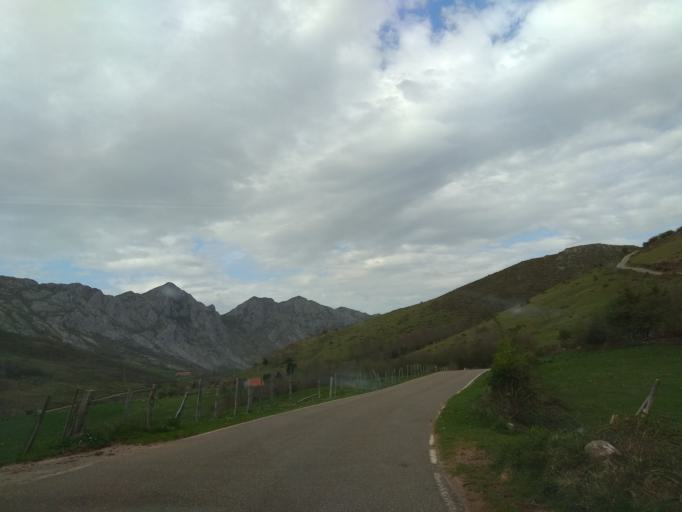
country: ES
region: Cantabria
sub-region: Provincia de Cantabria
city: Cabezon de Liebana
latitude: 43.2467
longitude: -4.5410
